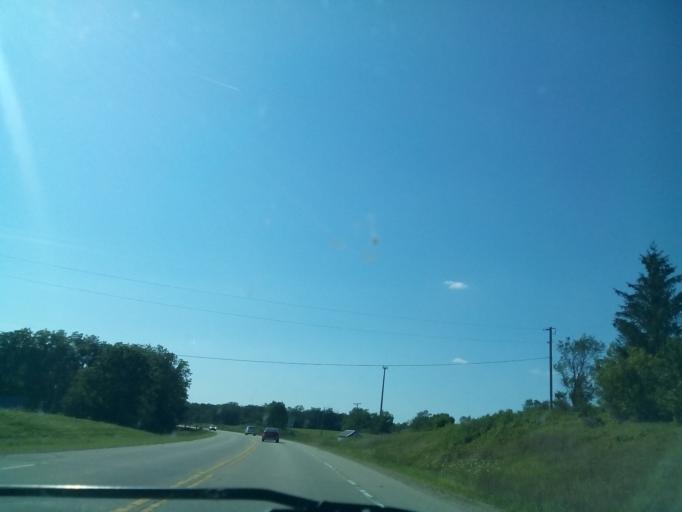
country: US
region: Wisconsin
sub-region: Dane County
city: Belleville
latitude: 42.8655
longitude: -89.5972
